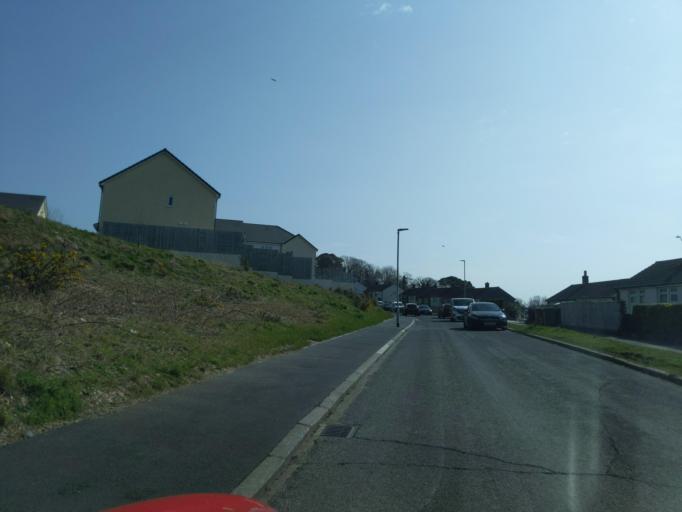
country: GB
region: England
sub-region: Plymouth
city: Plymouth
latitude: 50.4272
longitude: -4.1413
